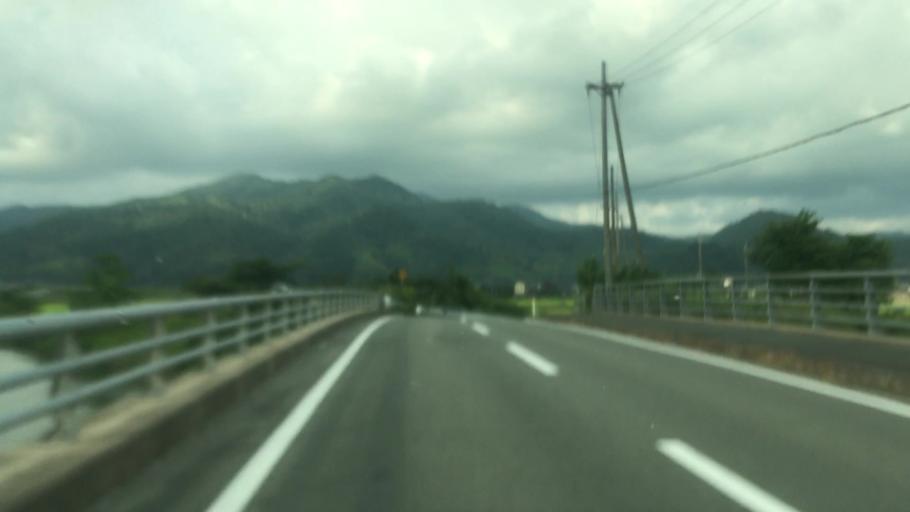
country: JP
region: Hyogo
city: Toyooka
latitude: 35.5644
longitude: 134.8053
